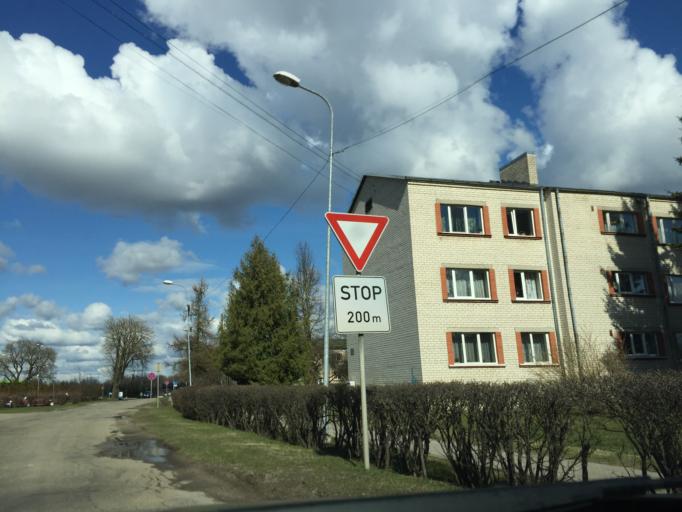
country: LV
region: Kekava
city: Kekava
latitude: 56.8300
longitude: 24.2322
